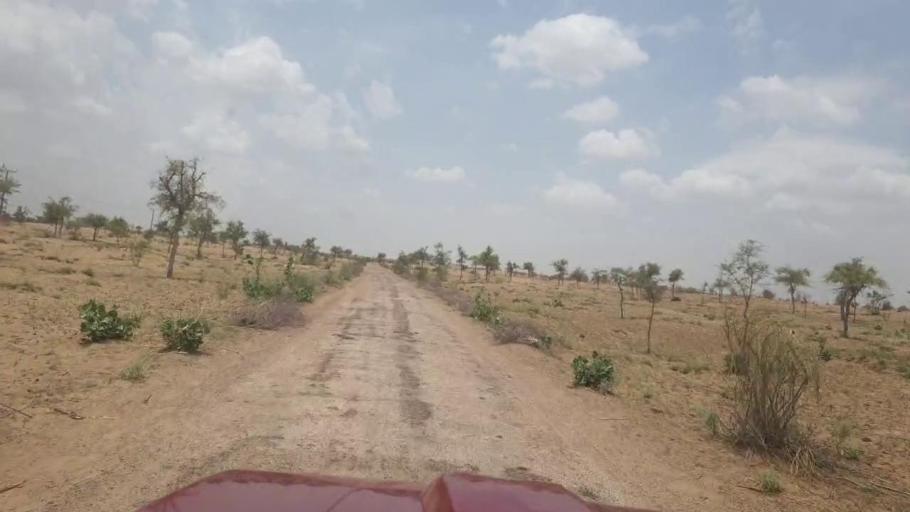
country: PK
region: Sindh
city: Islamkot
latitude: 25.2208
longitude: 70.4709
